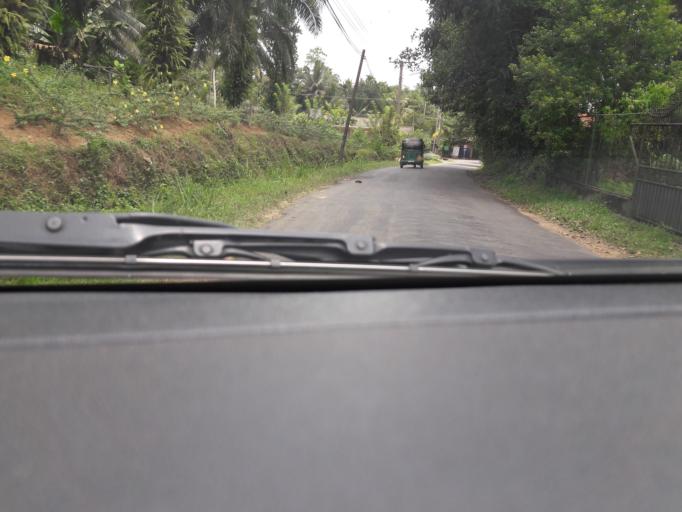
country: LK
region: Southern
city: Hikkaduwa
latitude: 6.2587
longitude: 80.2643
